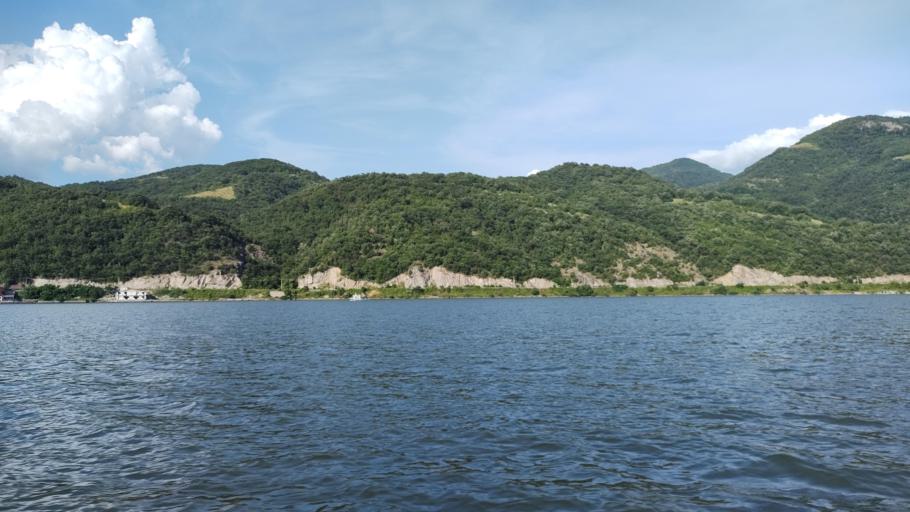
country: RO
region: Mehedinti
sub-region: Comuna Svinita
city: Svinita
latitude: 44.5308
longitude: 22.0675
